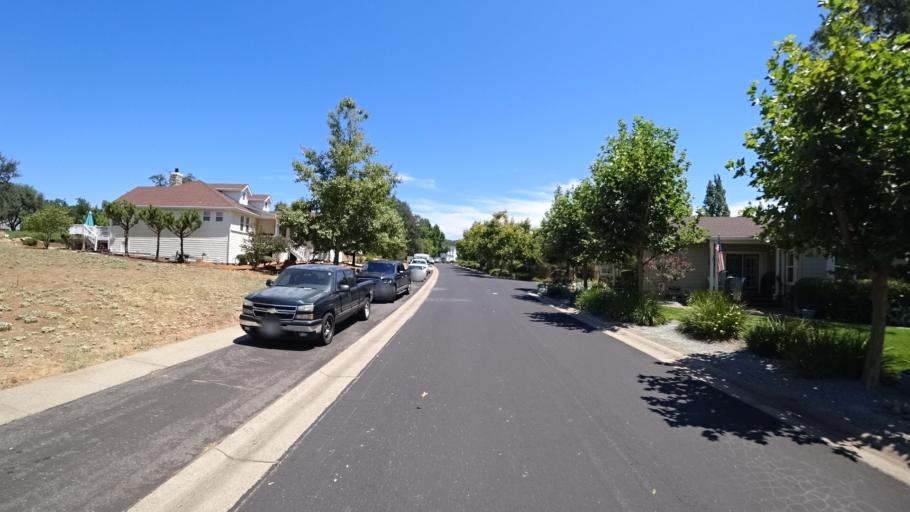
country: US
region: California
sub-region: Calaveras County
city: Angels Camp
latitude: 38.0662
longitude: -120.5558
